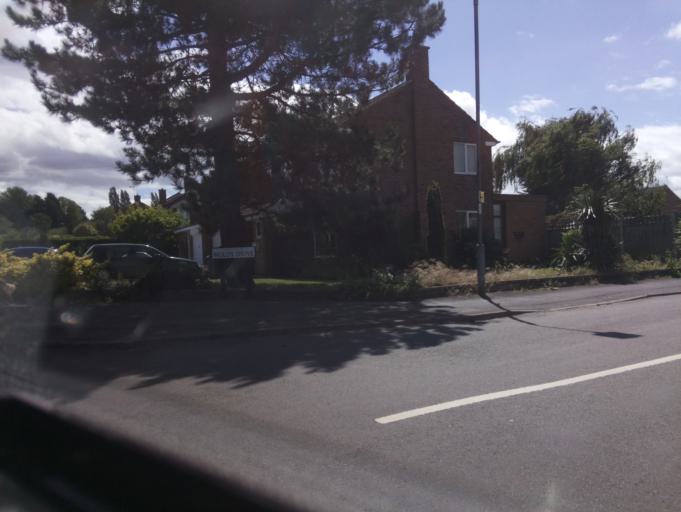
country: GB
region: England
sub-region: Nottinghamshire
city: Cotgrave
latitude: 52.8790
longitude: -1.0805
